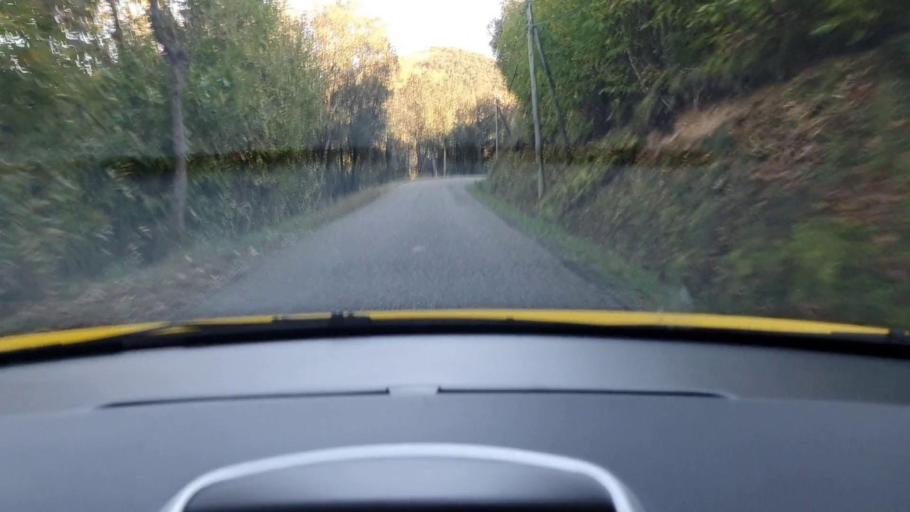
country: FR
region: Languedoc-Roussillon
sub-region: Departement du Gard
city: Sumene
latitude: 43.9887
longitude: 3.6835
